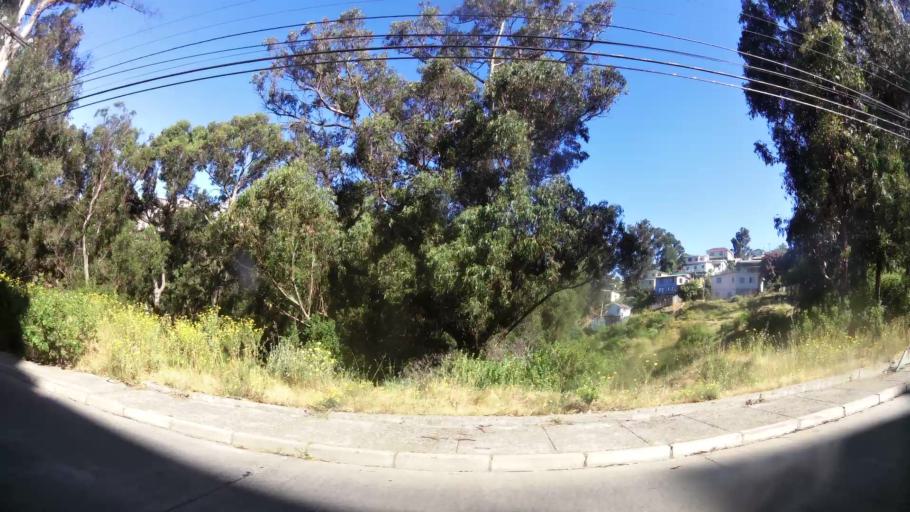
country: CL
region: Valparaiso
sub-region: Provincia de Valparaiso
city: Vina del Mar
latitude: -33.0366
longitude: -71.5628
